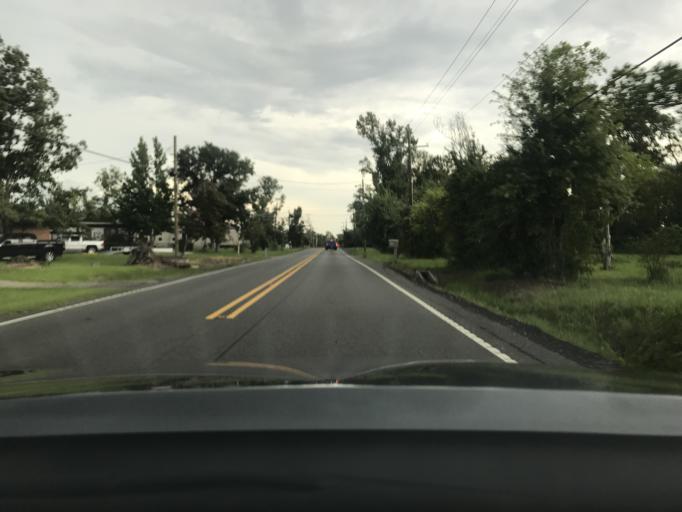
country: US
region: Louisiana
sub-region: Calcasieu Parish
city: Westlake
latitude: 30.2669
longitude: -93.2443
